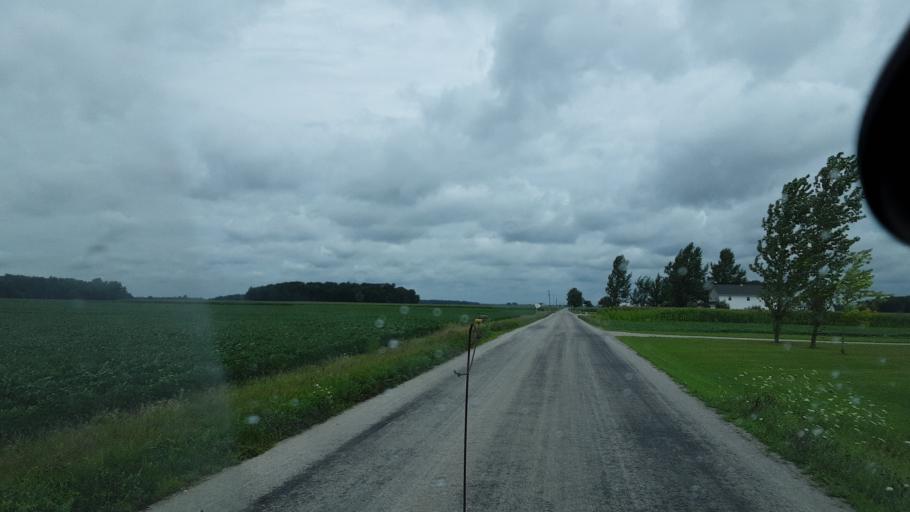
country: US
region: Indiana
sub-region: Adams County
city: Decatur
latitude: 40.7595
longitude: -84.9952
